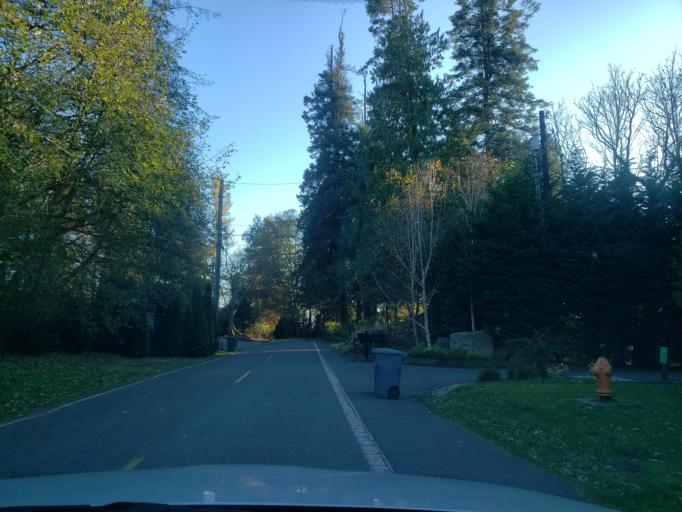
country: US
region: Washington
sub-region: Snohomish County
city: Woodway
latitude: 47.7788
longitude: -122.3883
